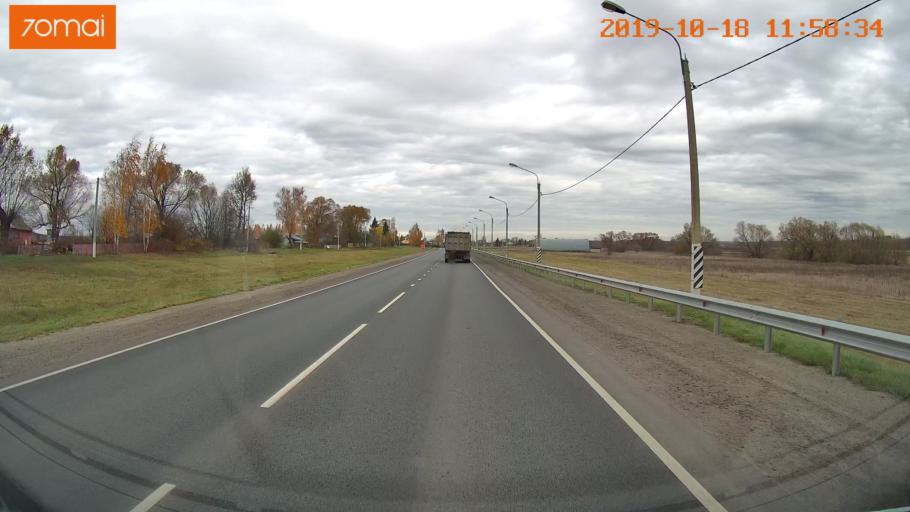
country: RU
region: Rjazan
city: Zakharovo
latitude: 54.2732
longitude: 39.1683
